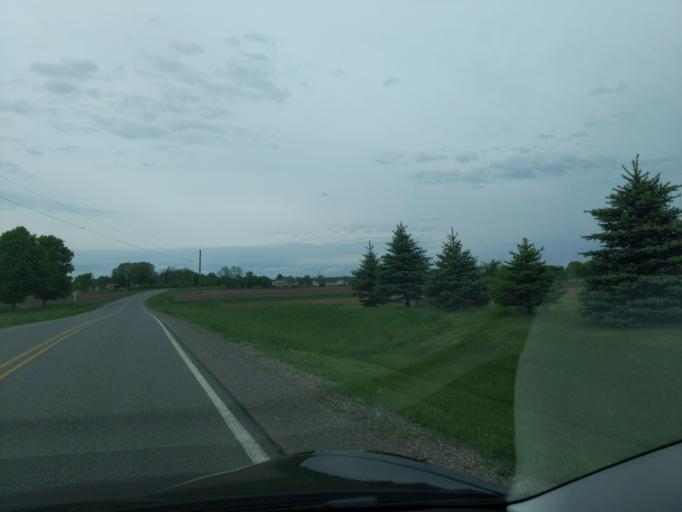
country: US
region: Michigan
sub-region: Ingham County
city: Leslie
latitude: 42.4882
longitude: -84.4257
